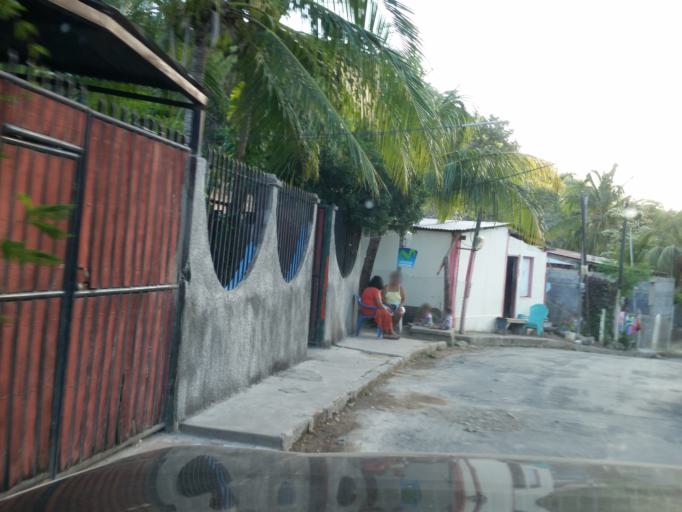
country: NI
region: Rivas
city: San Juan del Sur
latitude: 11.2479
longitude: -85.8737
